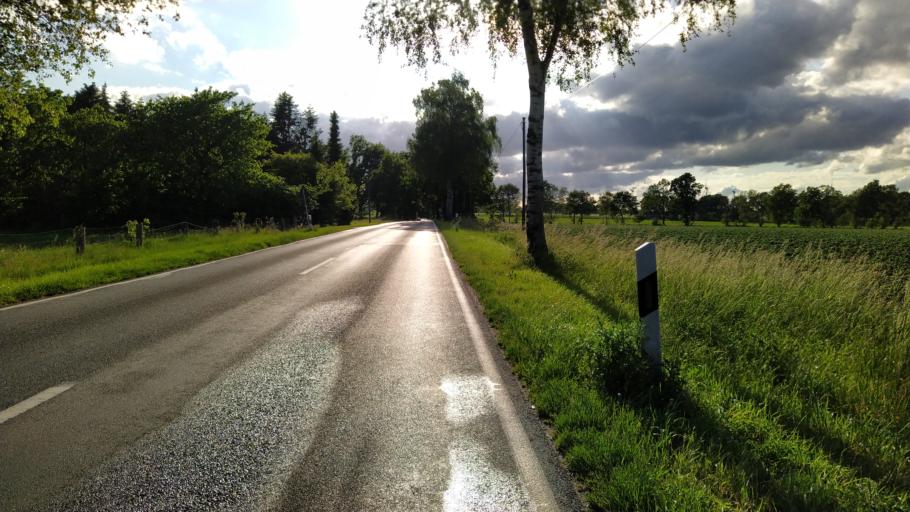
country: DE
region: Lower Saxony
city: Brest
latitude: 53.4645
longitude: 9.3973
